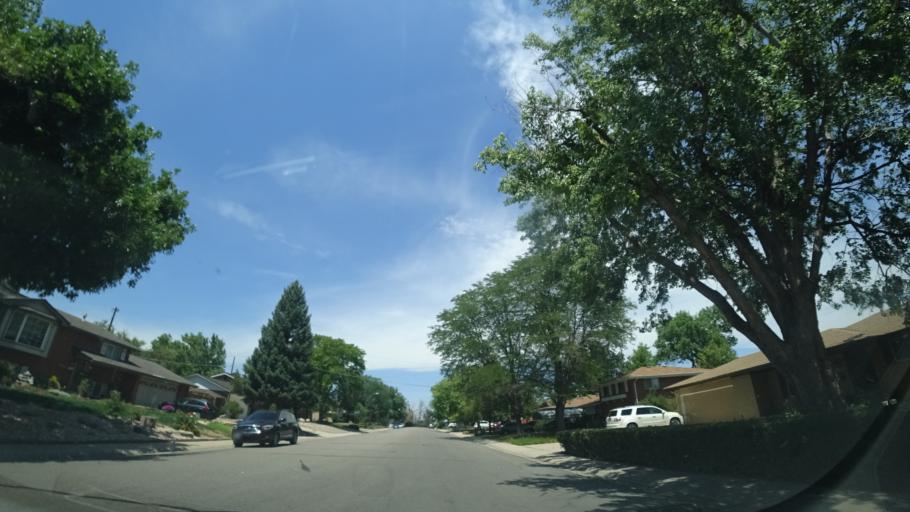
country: US
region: Colorado
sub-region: Jefferson County
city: Lakewood
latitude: 39.6947
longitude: -105.0895
